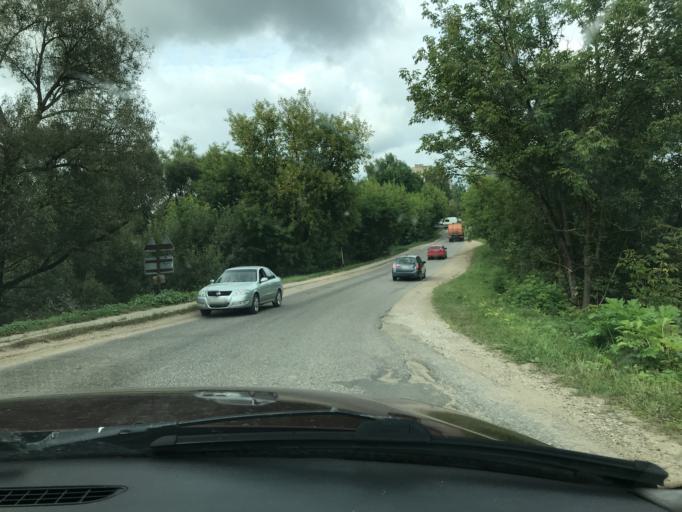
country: RU
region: Kaluga
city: Maloyaroslavets
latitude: 54.9971
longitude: 36.4707
